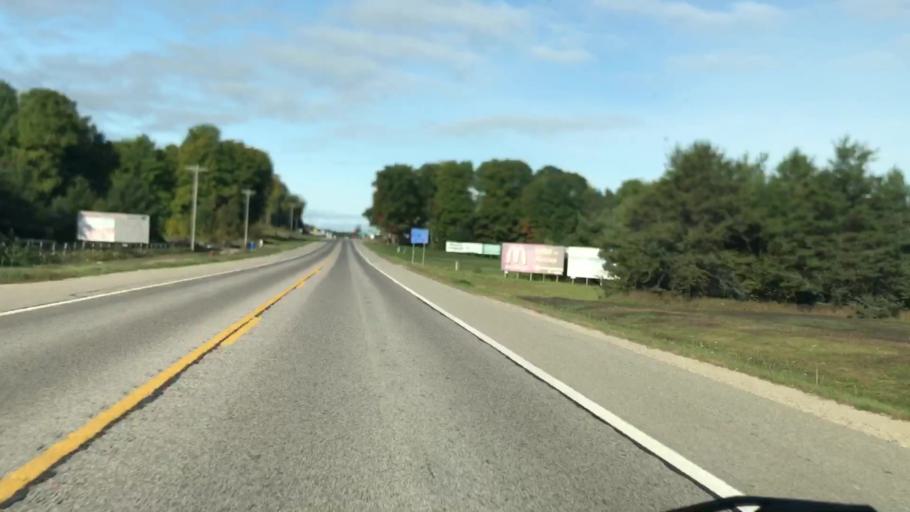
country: US
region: Michigan
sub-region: Luce County
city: Newberry
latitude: 46.3035
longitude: -85.5003
